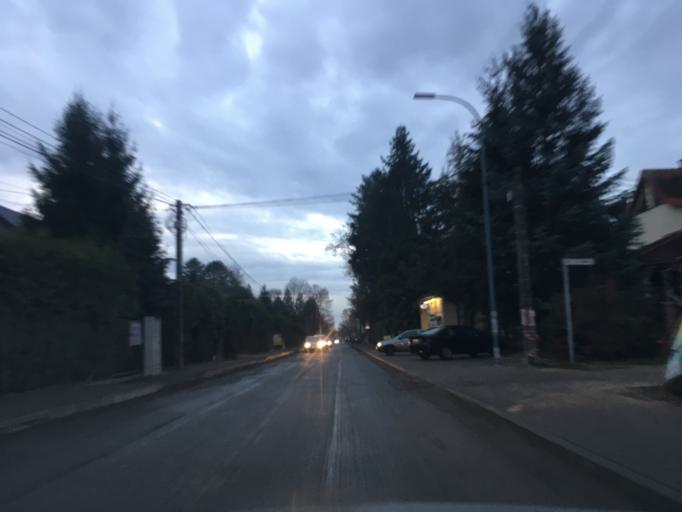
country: PL
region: Masovian Voivodeship
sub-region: Powiat piaseczynski
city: Piaseczno
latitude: 52.0539
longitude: 20.9853
